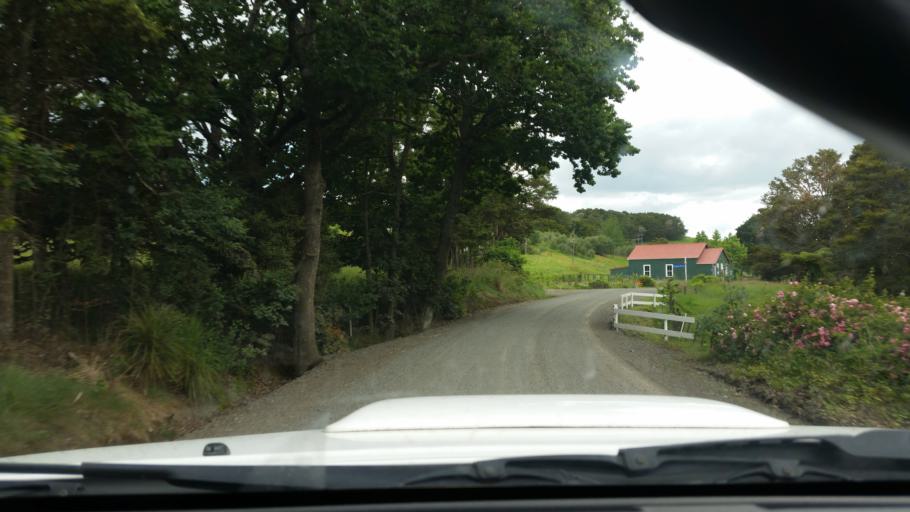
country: NZ
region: Northland
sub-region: Kaipara District
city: Dargaville
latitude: -35.8160
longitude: 173.9040
